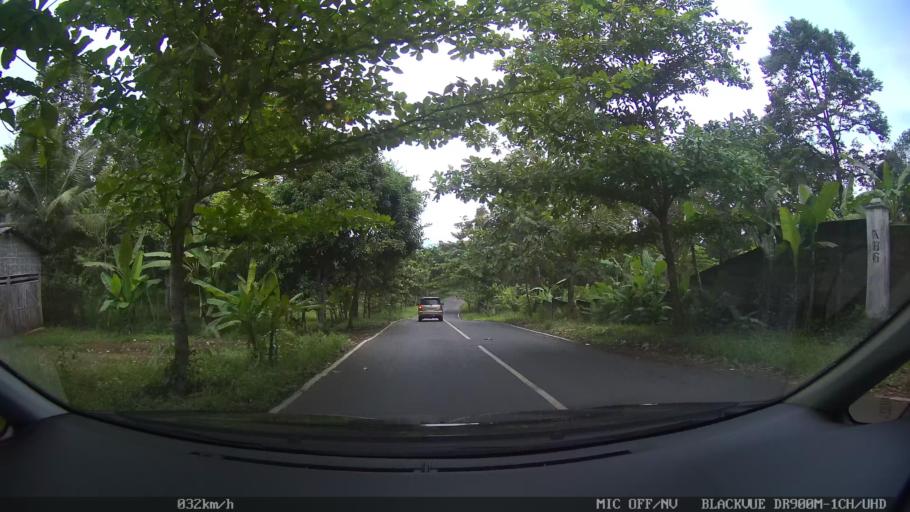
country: ID
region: Lampung
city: Bandarlampung
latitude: -5.4365
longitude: 105.2183
